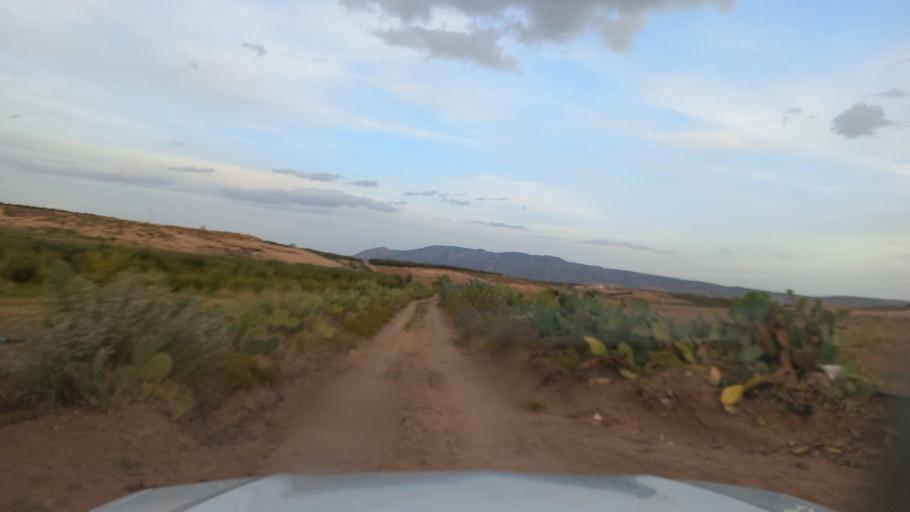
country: TN
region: Al Qasrayn
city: Sbiba
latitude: 35.4095
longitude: 9.0895
